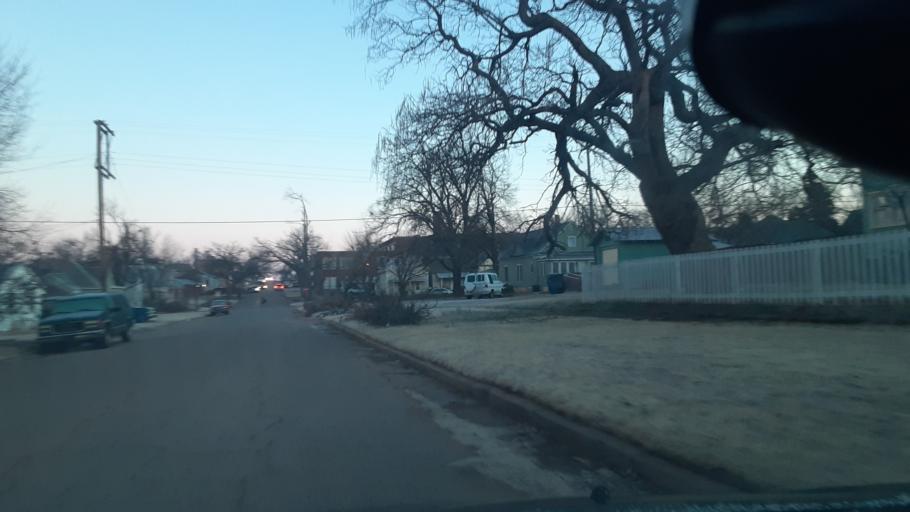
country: US
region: Oklahoma
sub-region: Logan County
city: Guthrie
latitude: 35.8761
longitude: -97.4176
